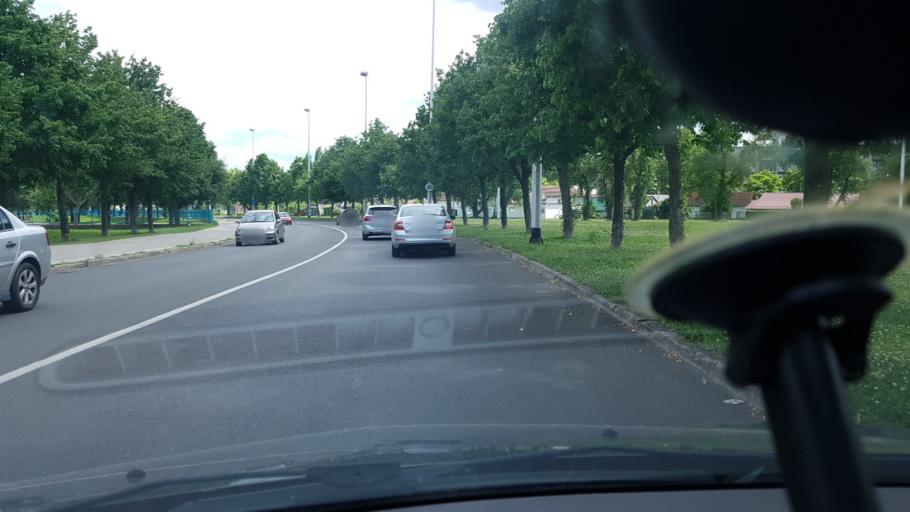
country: HR
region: Grad Zagreb
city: Novi Zagreb
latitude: 45.8046
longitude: 16.0252
